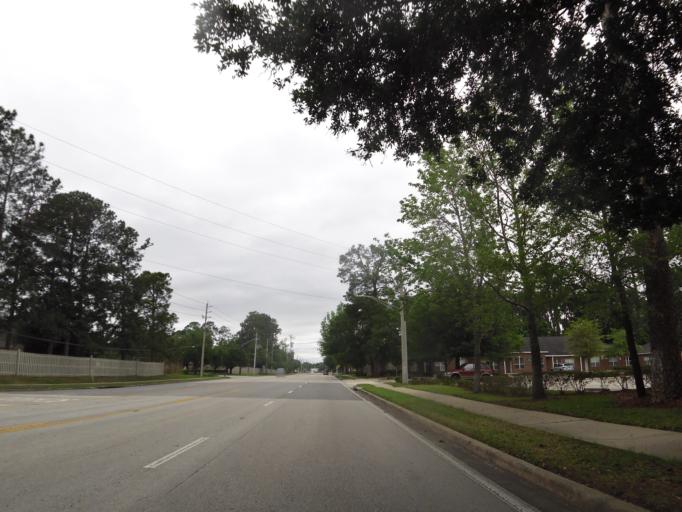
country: US
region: Florida
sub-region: Saint Johns County
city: Fruit Cove
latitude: 30.1967
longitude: -81.6130
